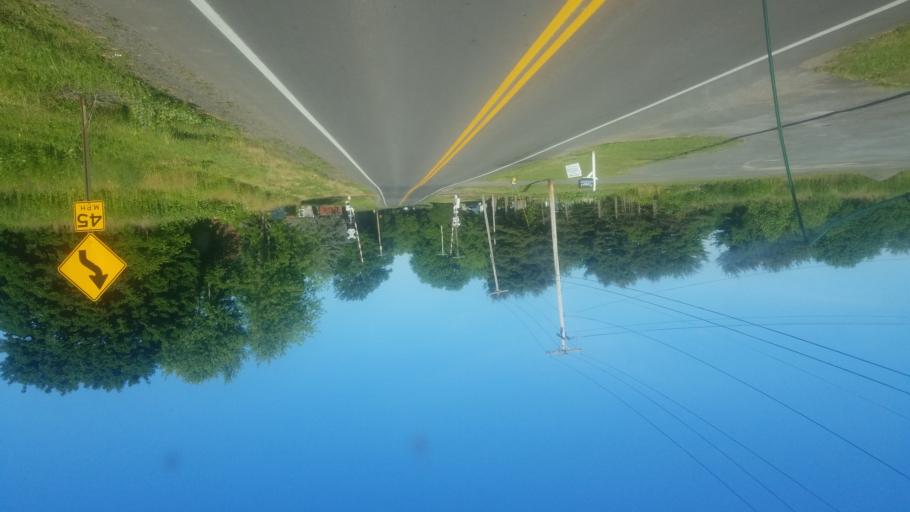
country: US
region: New York
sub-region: Wayne County
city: Newark
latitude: 43.0643
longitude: -77.0878
